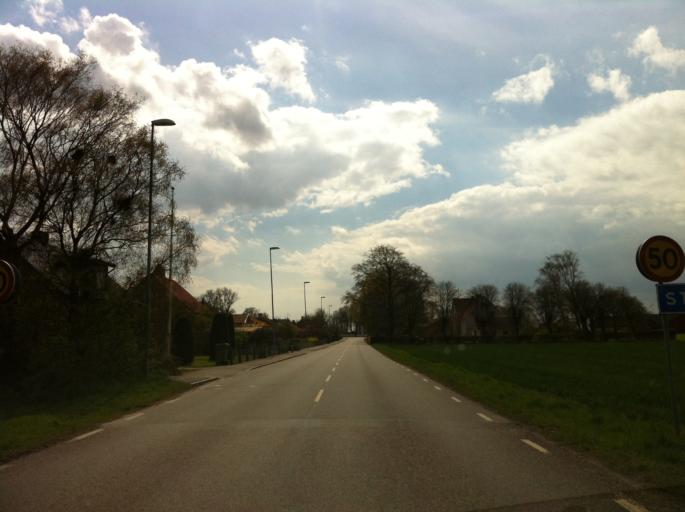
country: SE
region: Skane
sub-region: Kavlinge Kommun
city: Kaevlinge
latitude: 55.8078
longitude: 13.1581
